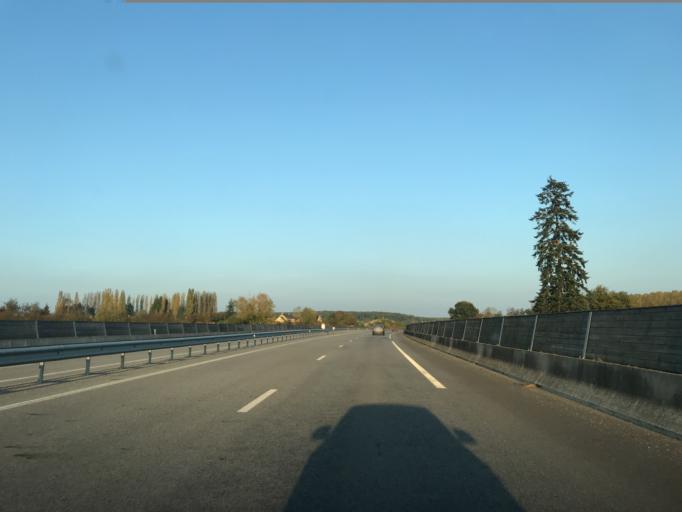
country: FR
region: Lower Normandy
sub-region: Departement de l'Orne
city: Valframbert
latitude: 48.4775
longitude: 0.2119
